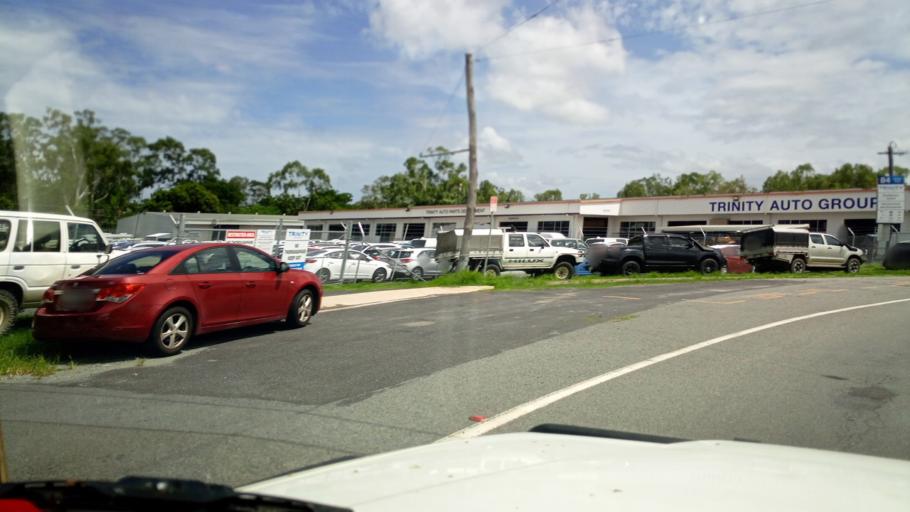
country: AU
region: Queensland
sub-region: Cairns
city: Woree
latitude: -16.9424
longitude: 145.7430
